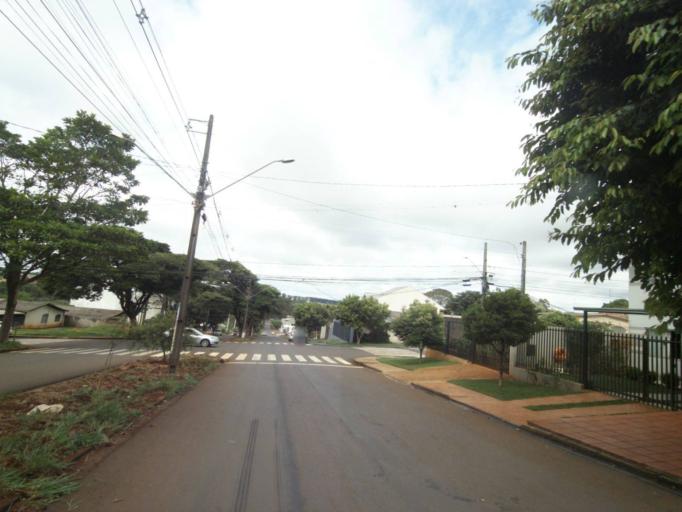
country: BR
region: Parana
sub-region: Campo Mourao
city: Campo Mourao
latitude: -24.0507
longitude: -52.3790
